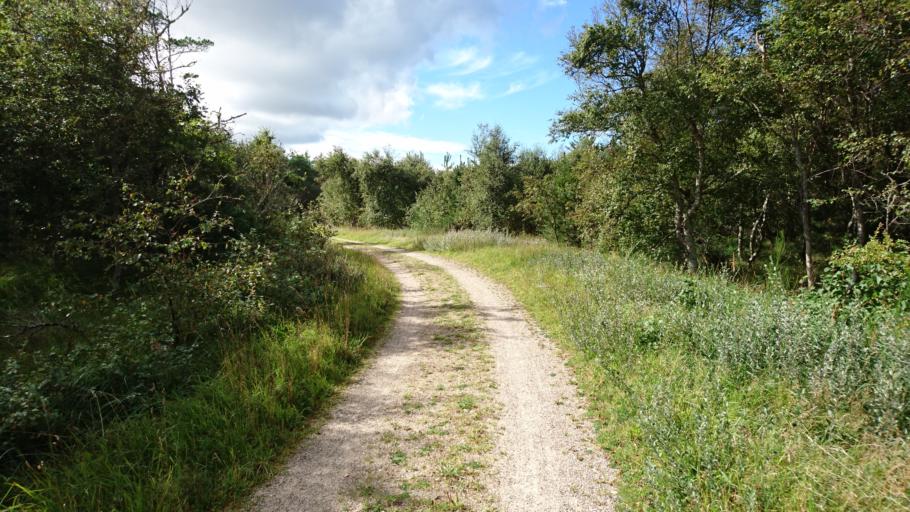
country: DK
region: North Denmark
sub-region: Frederikshavn Kommune
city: Skagen
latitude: 57.7157
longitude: 10.5186
